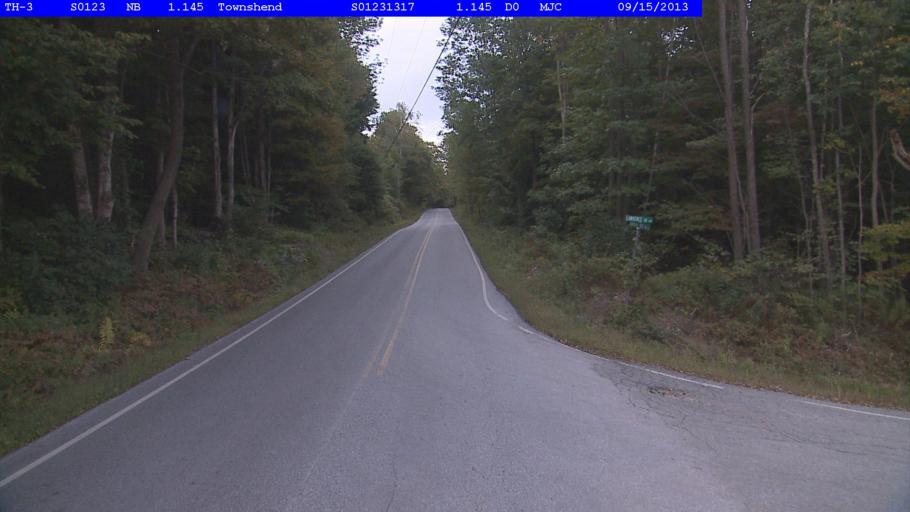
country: US
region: Vermont
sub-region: Windham County
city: Newfane
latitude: 43.0993
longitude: -72.7096
